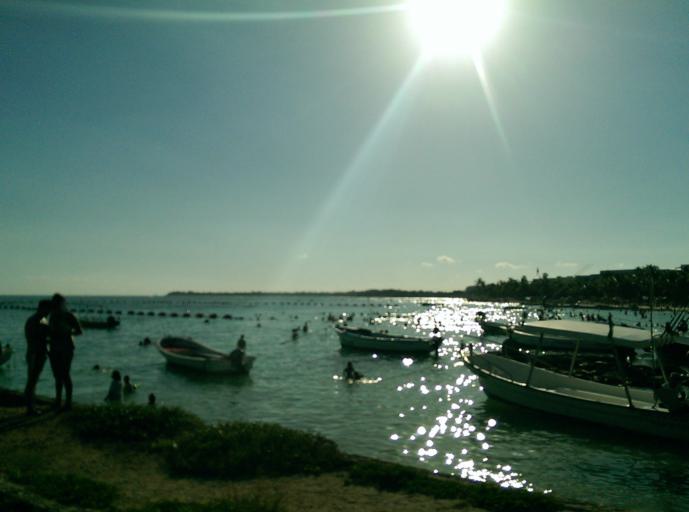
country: MX
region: Quintana Roo
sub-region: Tulum
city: Ciudad Chemuyil
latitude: 20.3962
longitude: -87.3130
